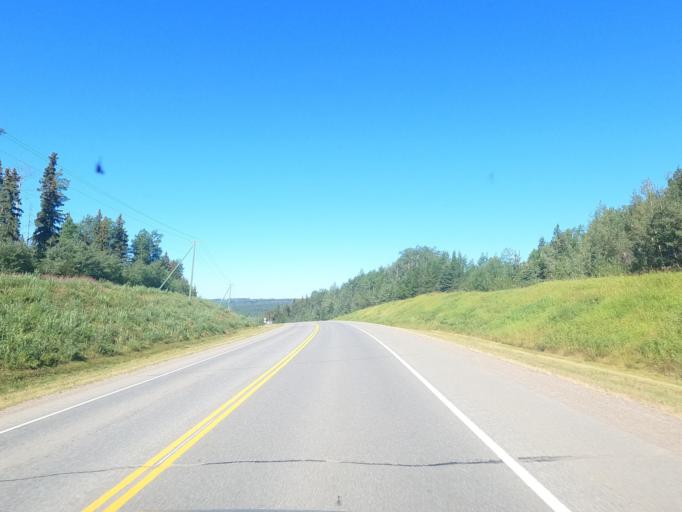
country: CA
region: British Columbia
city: Fort St. John
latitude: 56.6295
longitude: -121.5165
